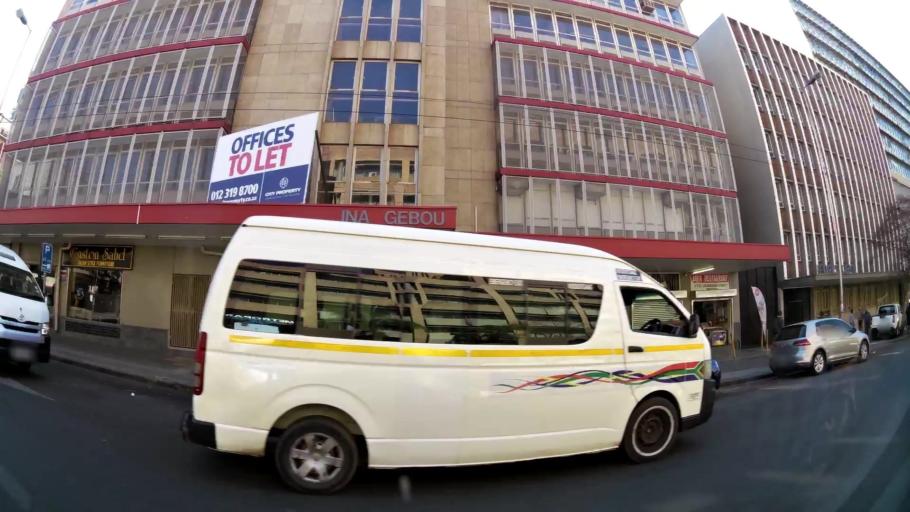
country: ZA
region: Gauteng
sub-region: City of Tshwane Metropolitan Municipality
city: Pretoria
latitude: -25.7488
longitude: 28.1959
